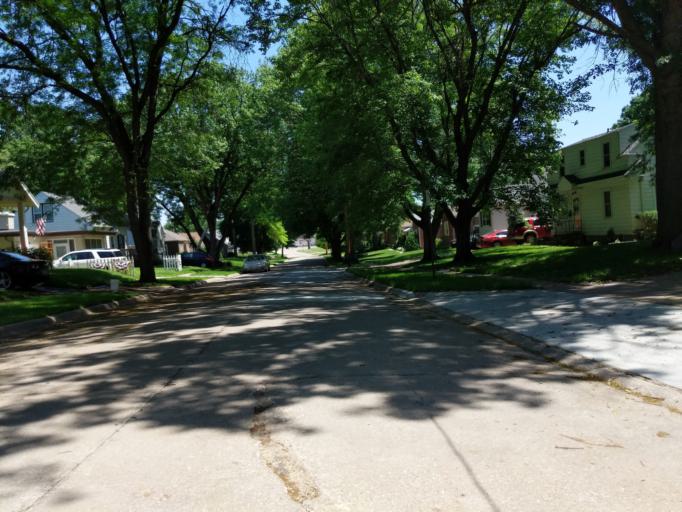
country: US
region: Iowa
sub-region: Linn County
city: Cedar Rapids
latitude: 42.0189
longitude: -91.6358
